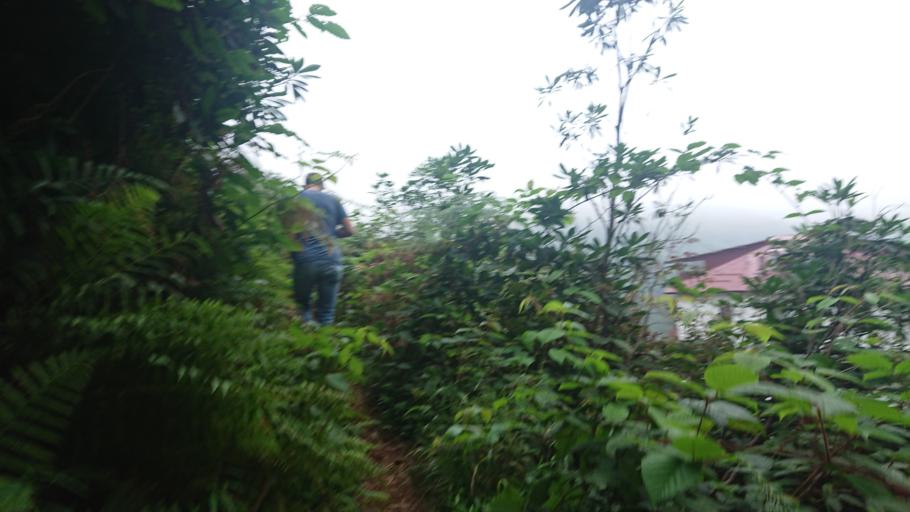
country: TR
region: Rize
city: Hemsin
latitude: 41.0459
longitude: 40.8084
